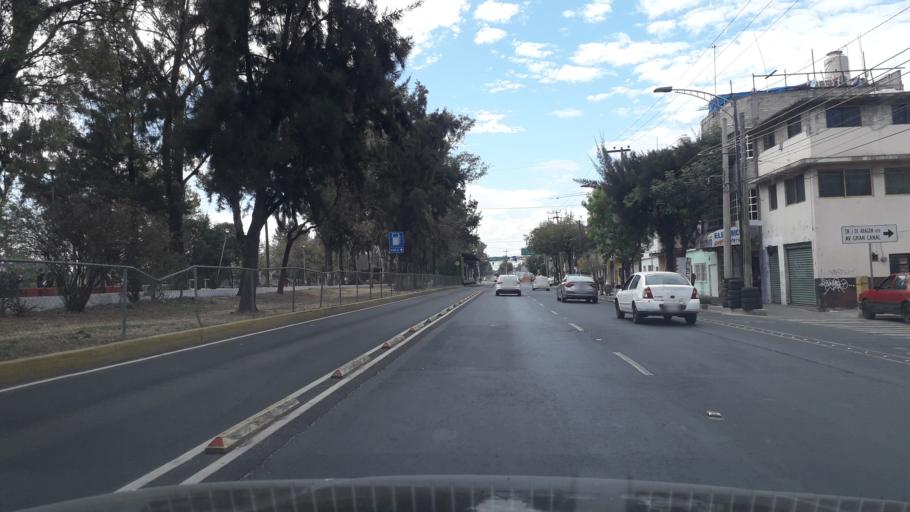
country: MX
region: Mexico City
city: Gustavo A. Madero
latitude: 19.4811
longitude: -99.0973
